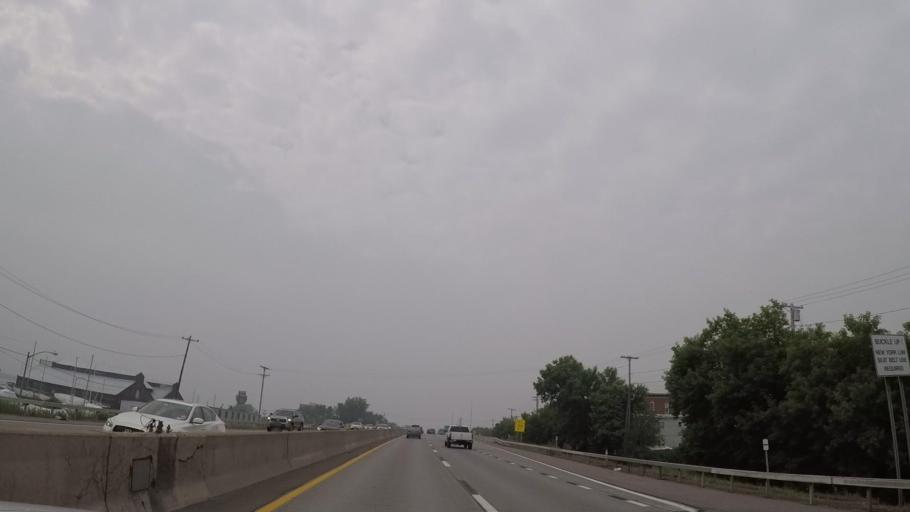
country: US
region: New York
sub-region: Erie County
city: Kenmore
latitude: 42.9355
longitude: -78.9038
